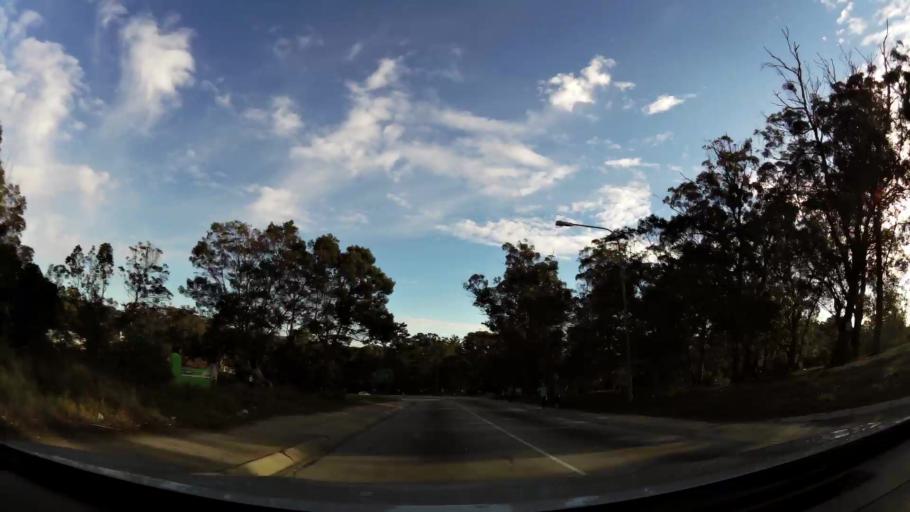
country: ZA
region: Eastern Cape
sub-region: Nelson Mandela Bay Metropolitan Municipality
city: Port Elizabeth
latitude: -33.9569
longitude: 25.5154
